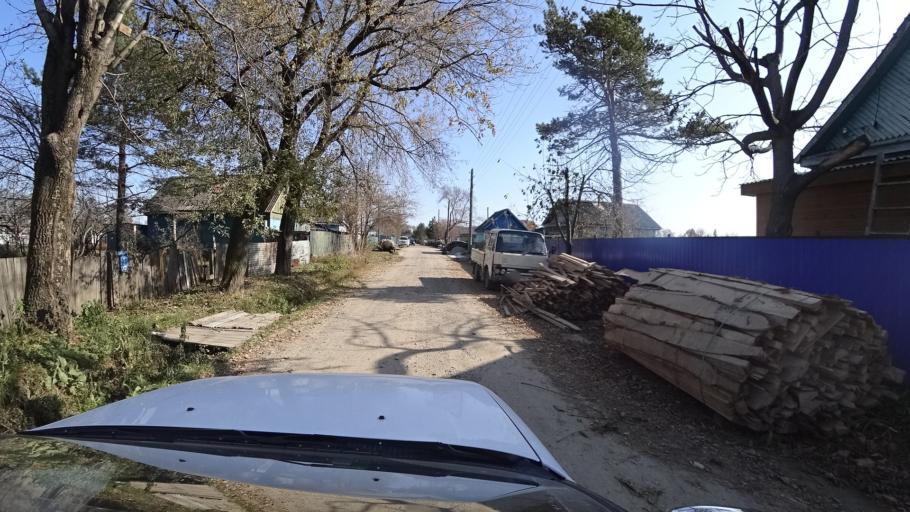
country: RU
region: Primorskiy
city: Dal'nerechensk
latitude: 45.9275
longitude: 133.7170
